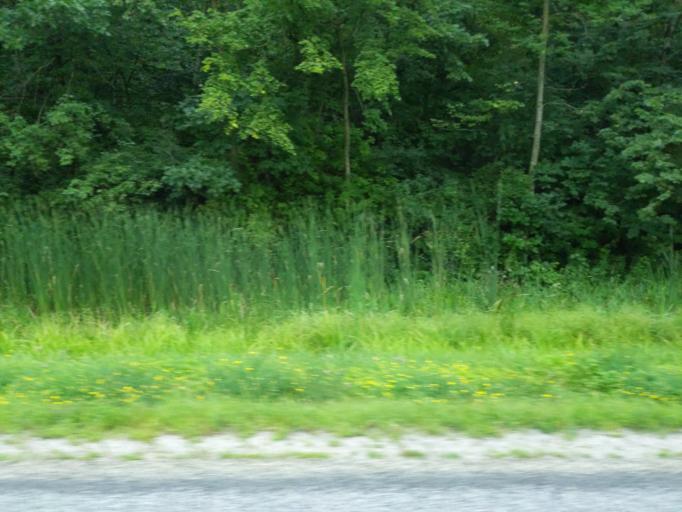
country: US
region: Wisconsin
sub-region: Sauk County
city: Sauk City
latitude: 43.2355
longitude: -89.7320
